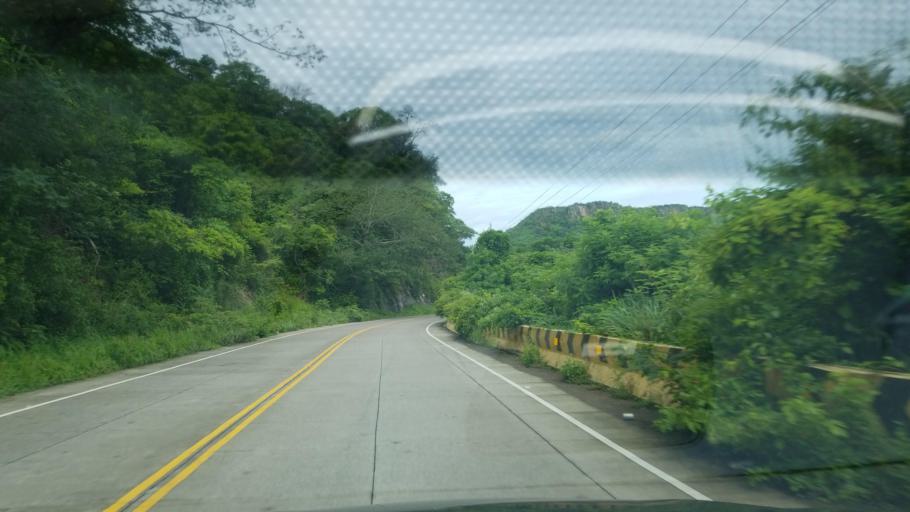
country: HN
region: Francisco Morazan
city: El Porvenir
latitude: 13.6850
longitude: -87.3524
